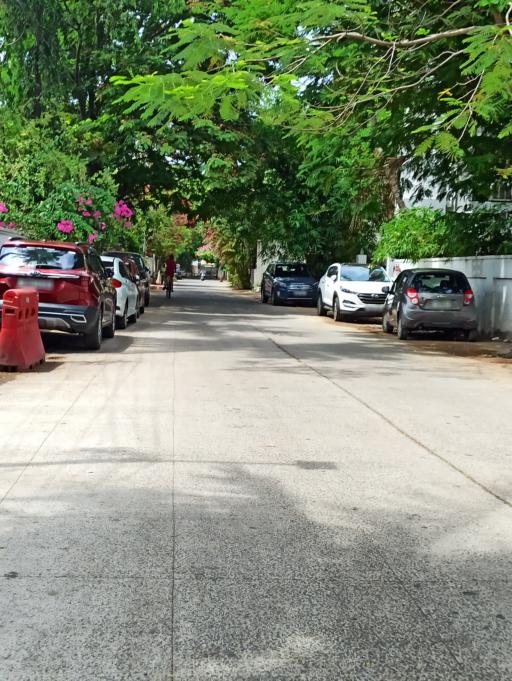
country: IN
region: Tamil Nadu
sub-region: Chennai
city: Chetput
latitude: 13.0714
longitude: 80.2396
